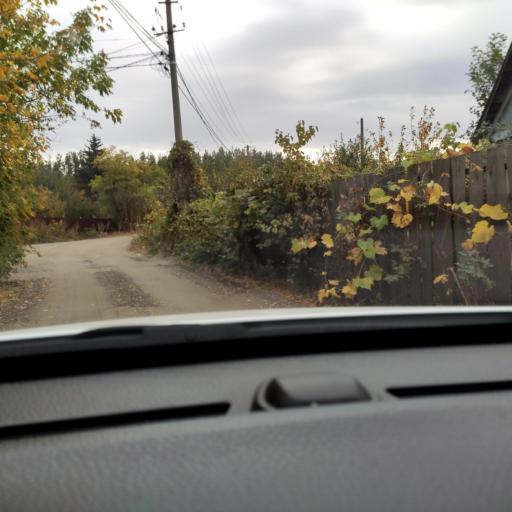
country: RU
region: Voronezj
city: Maslovka
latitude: 51.6035
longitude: 39.2778
